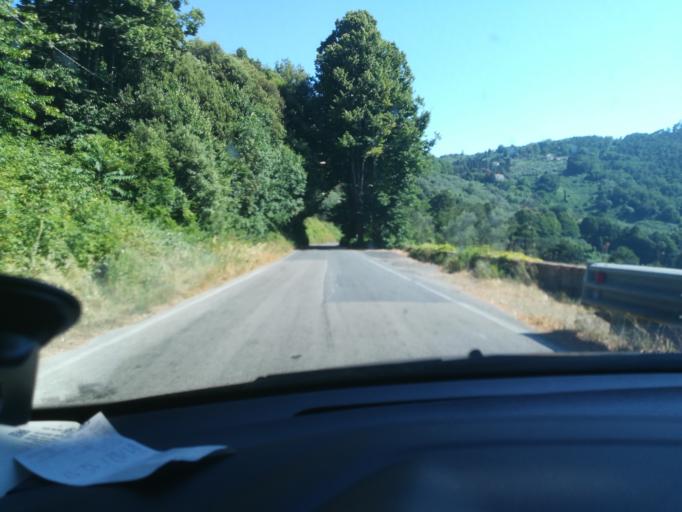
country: IT
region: Tuscany
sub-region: Provincia di Lucca
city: Stiava
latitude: 43.9176
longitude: 10.3390
